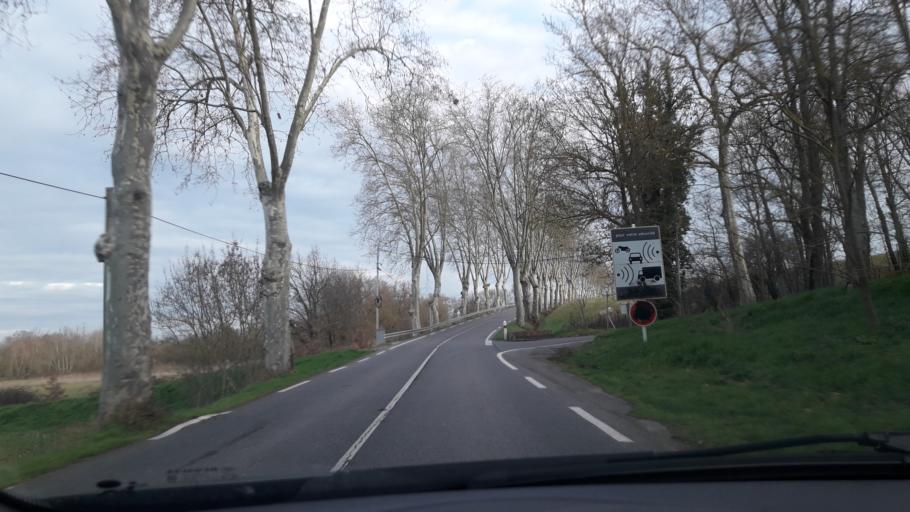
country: FR
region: Midi-Pyrenees
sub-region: Departement de la Haute-Garonne
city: Grenade
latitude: 43.7451
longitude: 1.2650
